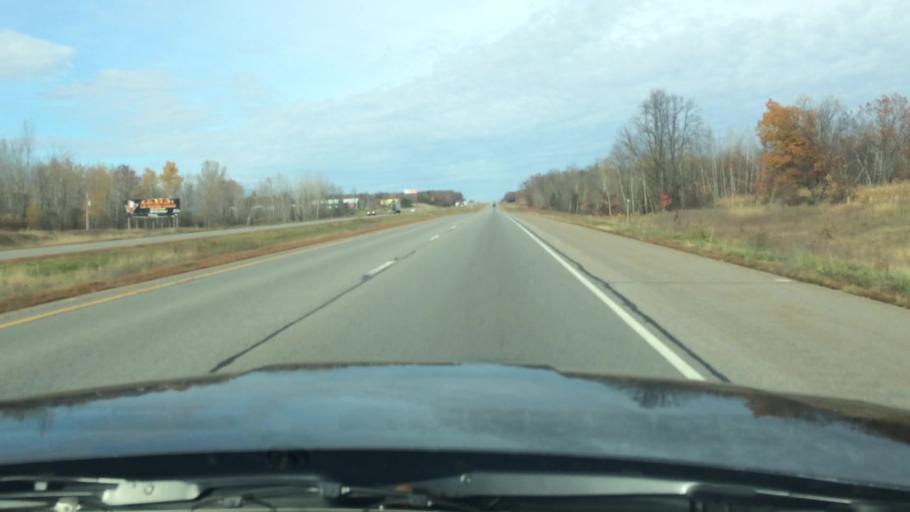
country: US
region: Wisconsin
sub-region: Marathon County
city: Mosinee
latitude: 44.7519
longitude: -89.6798
